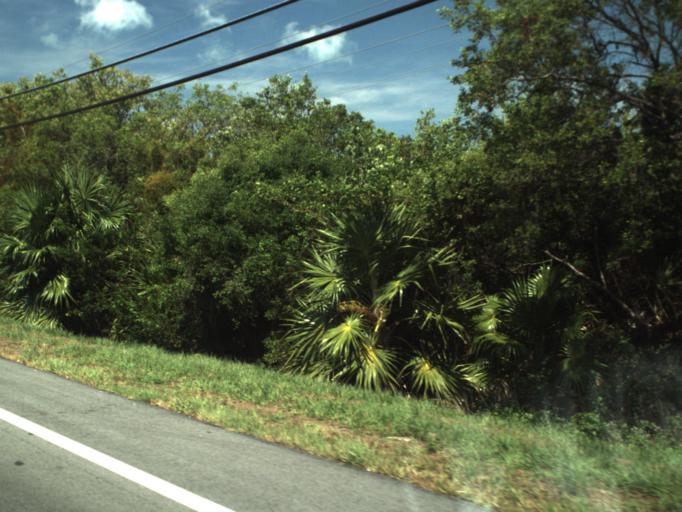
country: US
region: Florida
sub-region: Monroe County
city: Marathon
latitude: 24.7456
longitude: -80.9854
